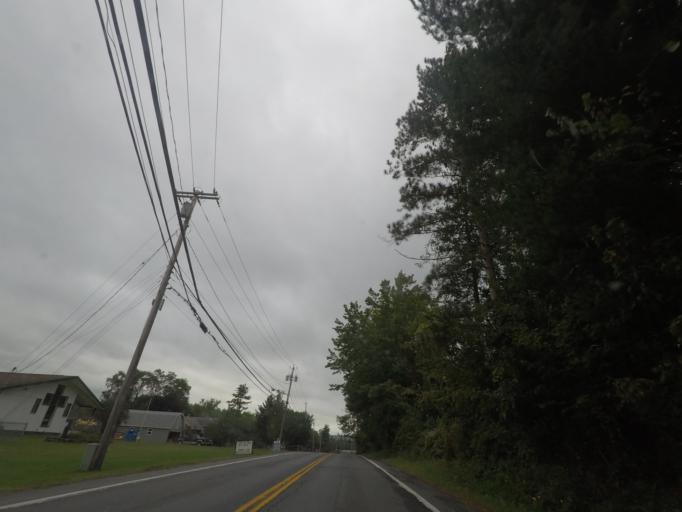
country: US
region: New York
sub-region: Rensselaer County
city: Hoosick Falls
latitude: 42.9199
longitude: -73.3495
